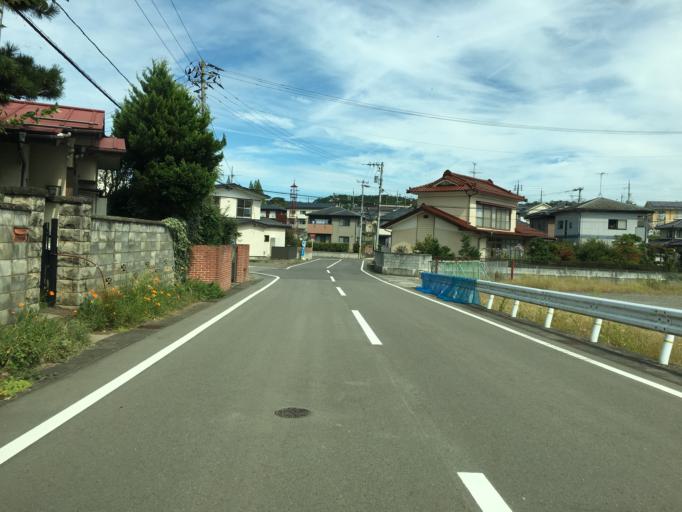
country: JP
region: Fukushima
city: Fukushima-shi
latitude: 37.6783
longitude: 140.4522
